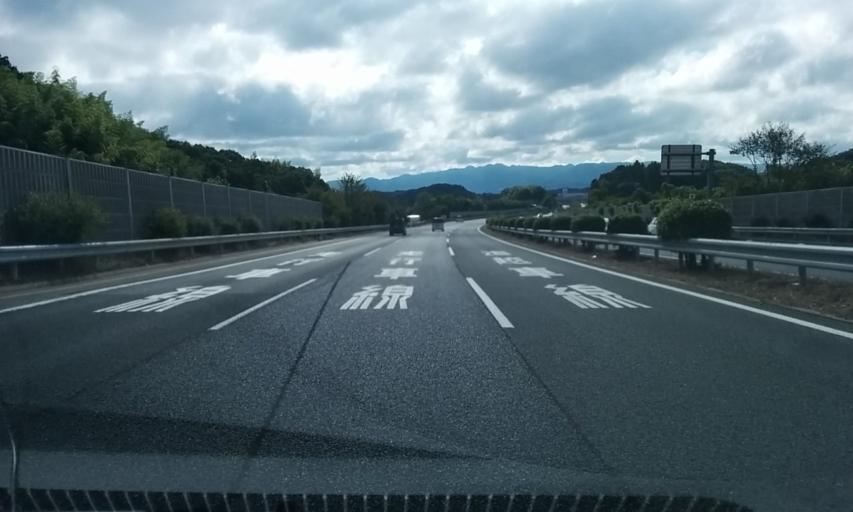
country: JP
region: Hyogo
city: Sandacho
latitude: 34.8764
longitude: 135.1942
